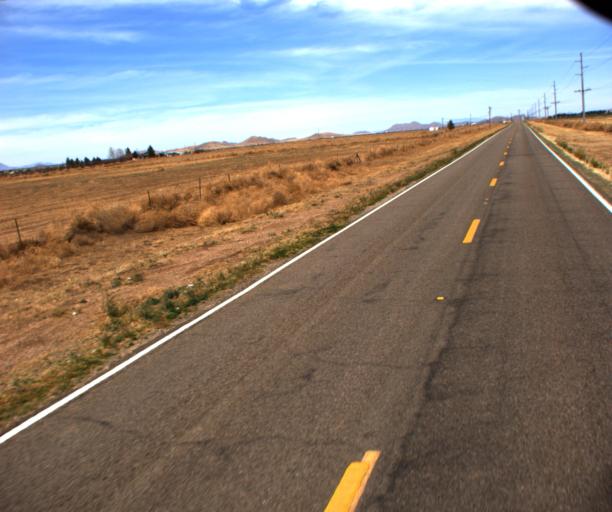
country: US
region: Arizona
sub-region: Cochise County
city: Tombstone
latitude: 31.8060
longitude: -109.6939
